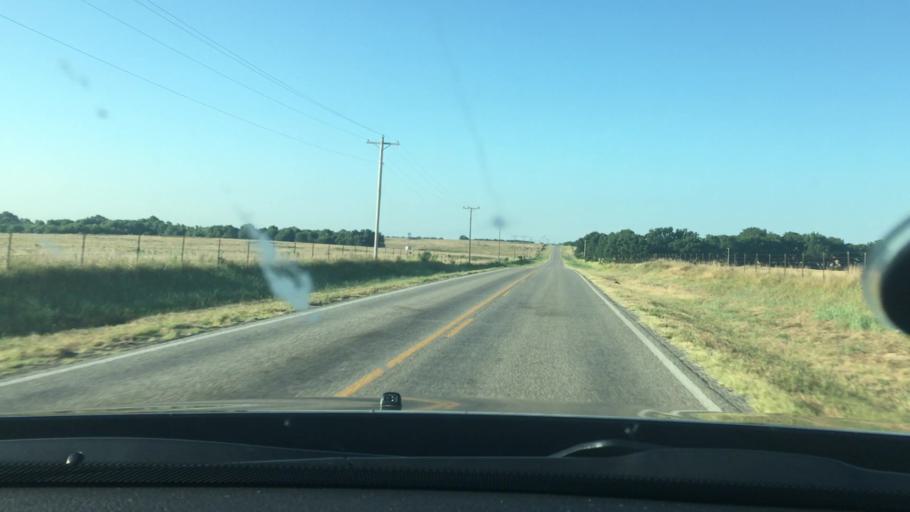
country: US
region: Oklahoma
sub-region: Murray County
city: Sulphur
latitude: 34.5915
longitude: -96.8449
